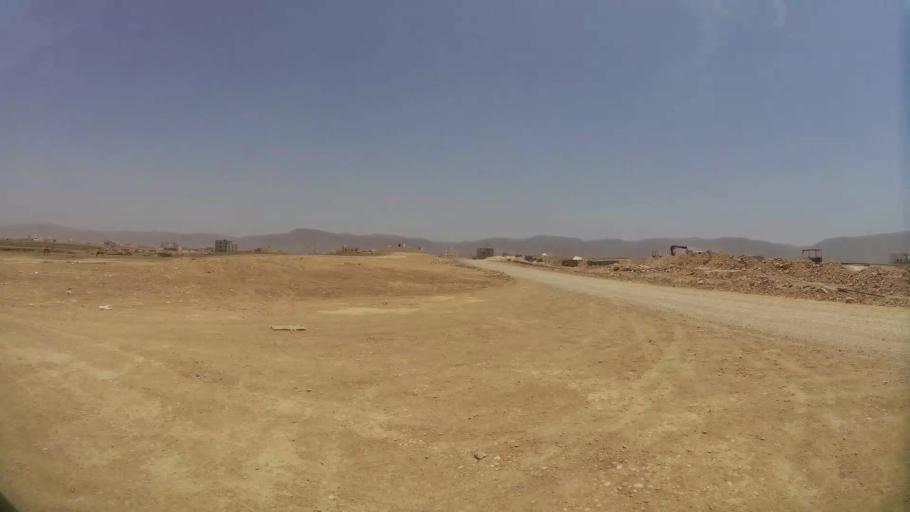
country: OM
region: Zufar
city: Salalah
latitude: 17.0951
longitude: 54.2057
